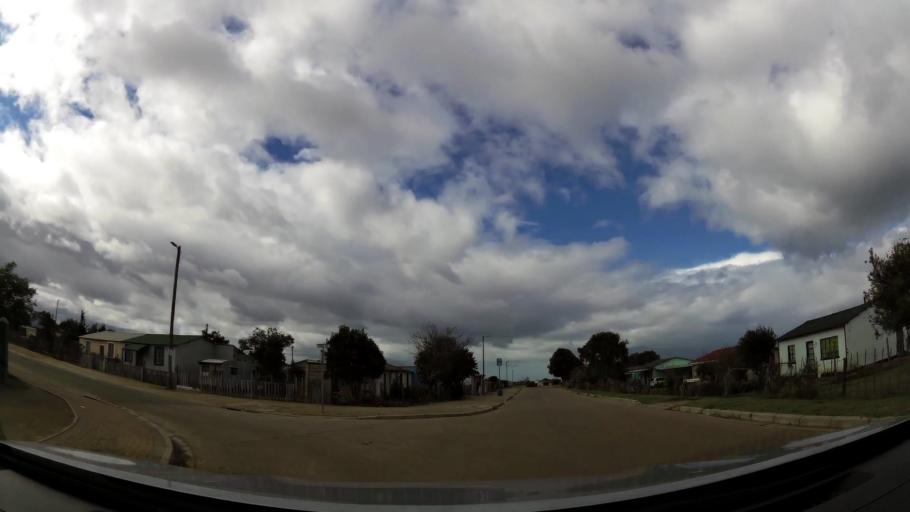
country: ZA
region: Western Cape
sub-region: Eden District Municipality
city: George
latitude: -34.0230
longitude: 22.4657
